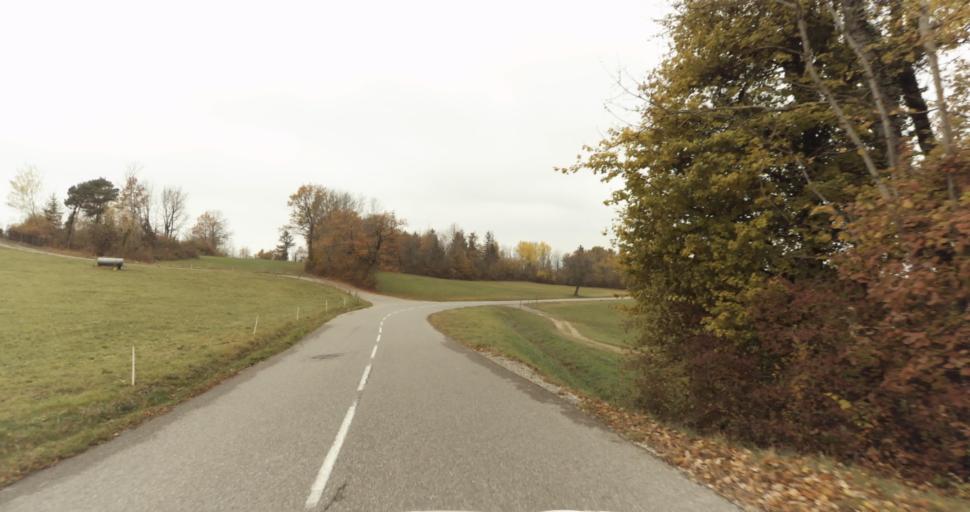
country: FR
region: Rhone-Alpes
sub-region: Departement de la Haute-Savoie
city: Seynod
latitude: 45.8515
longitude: 6.0845
